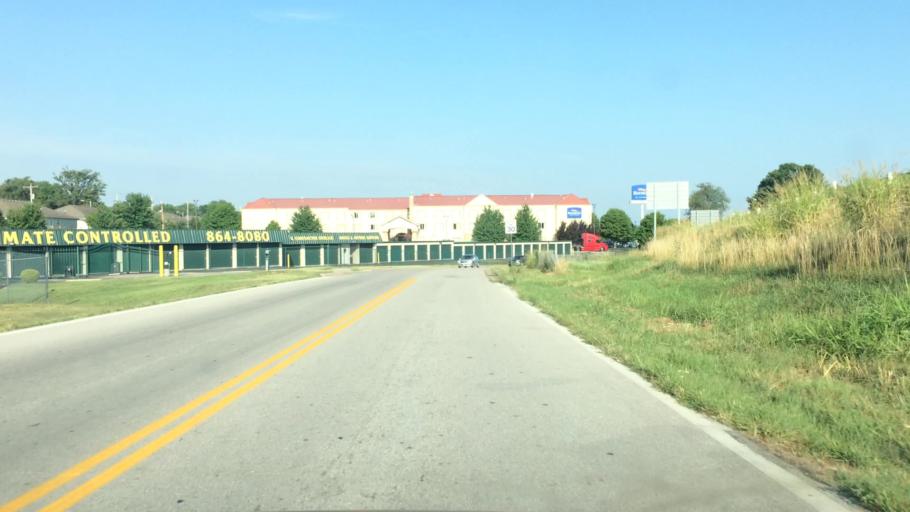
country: US
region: Missouri
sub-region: Greene County
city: Springfield
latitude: 37.2486
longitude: -93.2627
